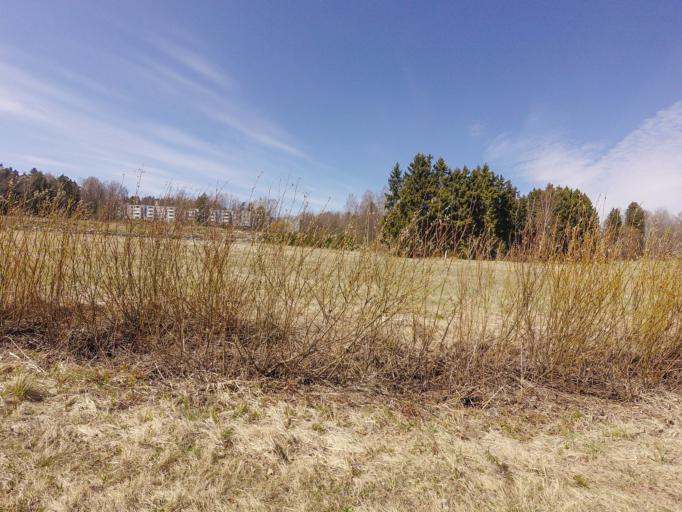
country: FI
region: Uusimaa
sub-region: Helsinki
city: Vantaa
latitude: 60.2354
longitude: 25.1347
